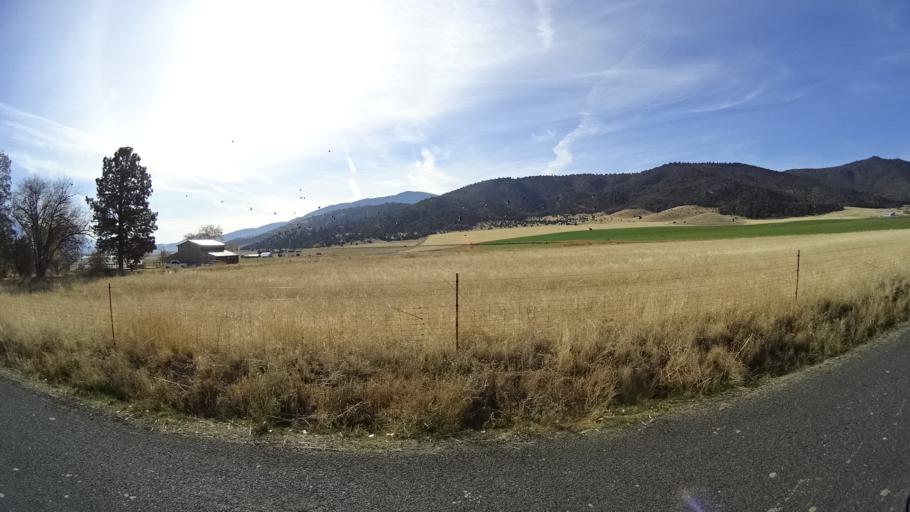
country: US
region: California
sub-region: Siskiyou County
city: Montague
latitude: 41.5382
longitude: -122.5500
